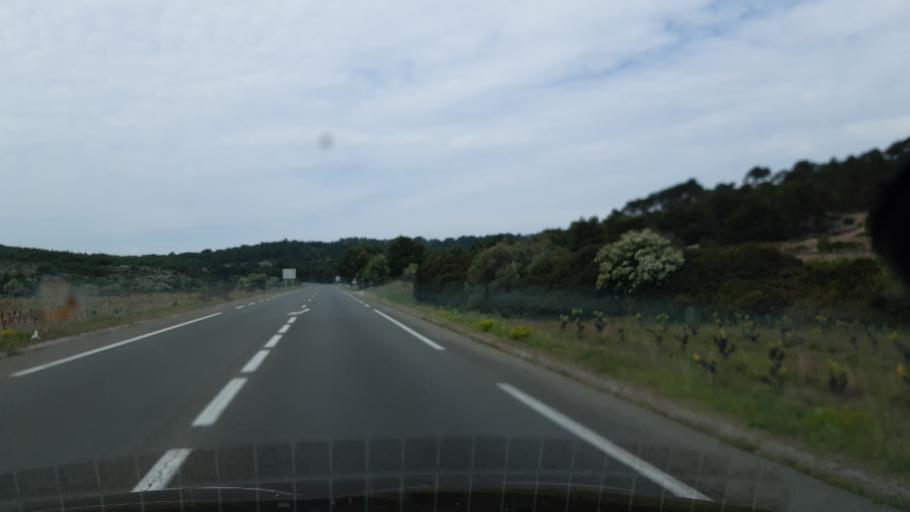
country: FR
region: Languedoc-Roussillon
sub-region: Departement de l'Aude
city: Gruissan
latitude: 43.1181
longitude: 3.0866
